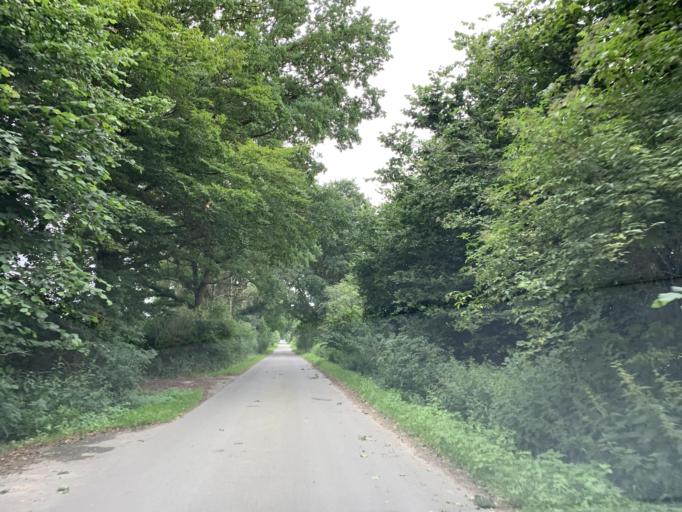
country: DE
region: Mecklenburg-Vorpommern
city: Blankensee
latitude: 53.4219
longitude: 13.2681
